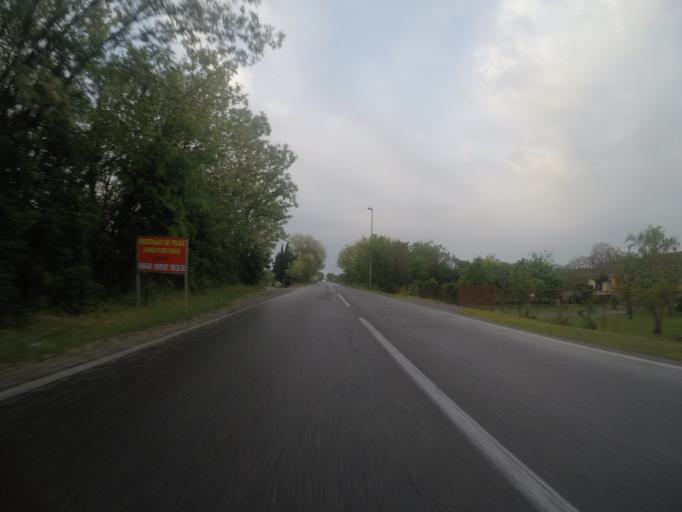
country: ME
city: Mojanovici
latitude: 42.3392
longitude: 19.2214
